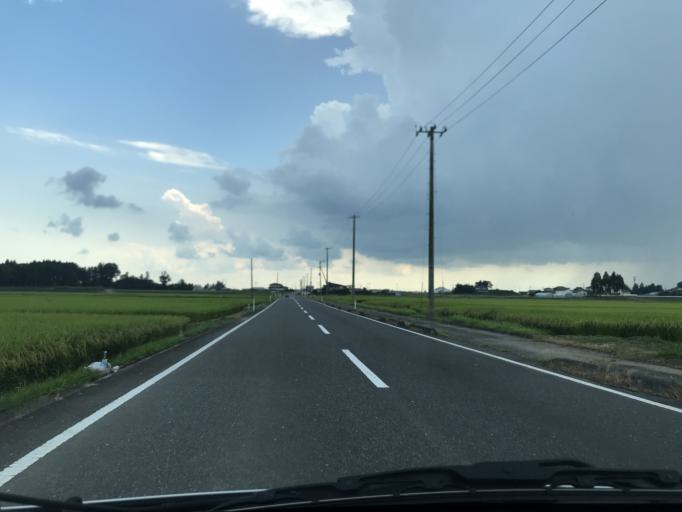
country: JP
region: Iwate
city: Ichinoseki
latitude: 38.7663
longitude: 141.0697
